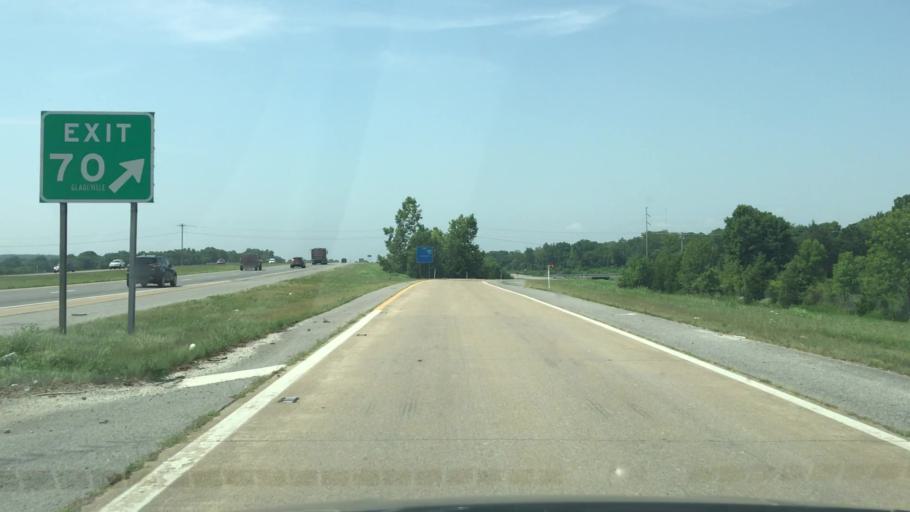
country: US
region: Tennessee
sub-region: Wilson County
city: Rural Hill
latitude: 36.1152
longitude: -86.4087
